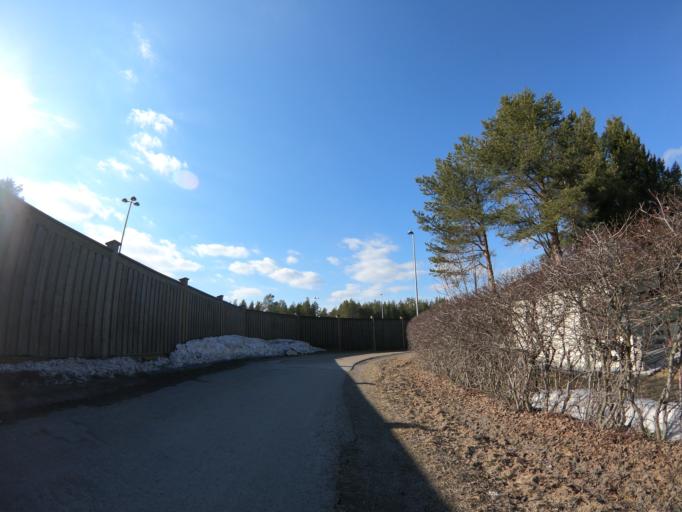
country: SE
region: Vaesterbotten
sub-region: Umea Kommun
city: Umea
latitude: 63.8056
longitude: 20.3228
